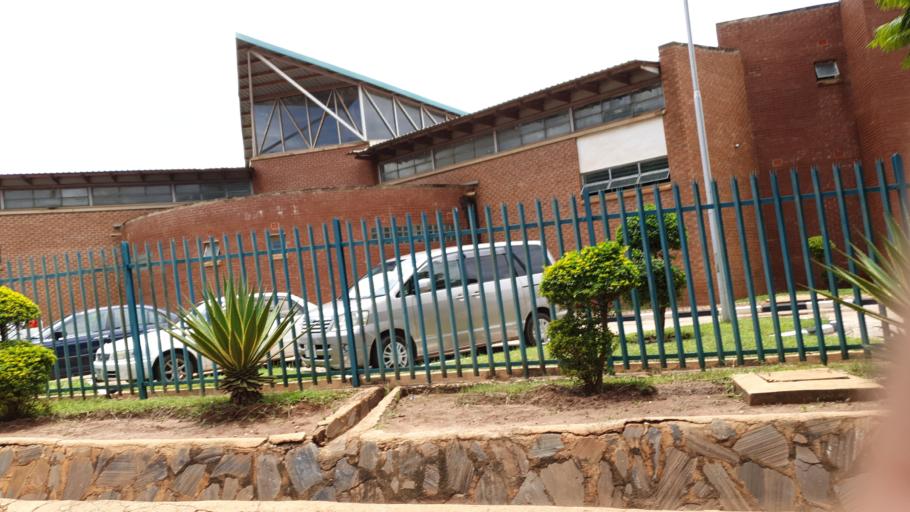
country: ZM
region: Lusaka
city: Lusaka
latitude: -15.4306
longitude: 28.3087
